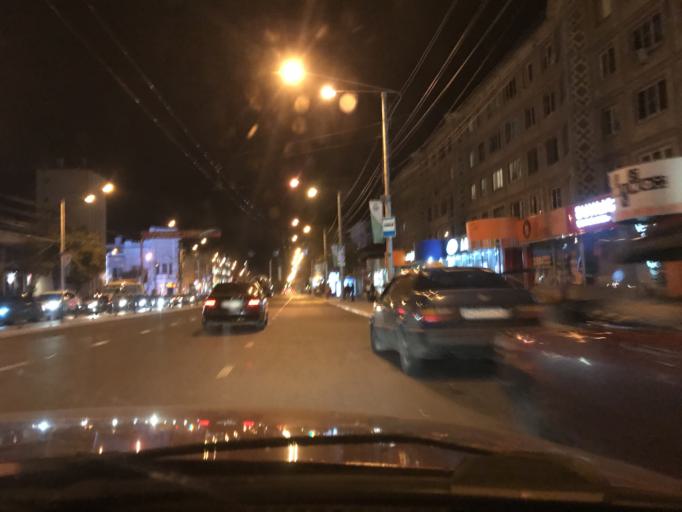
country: RU
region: Kaluga
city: Kaluga
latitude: 54.5137
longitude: 36.2616
